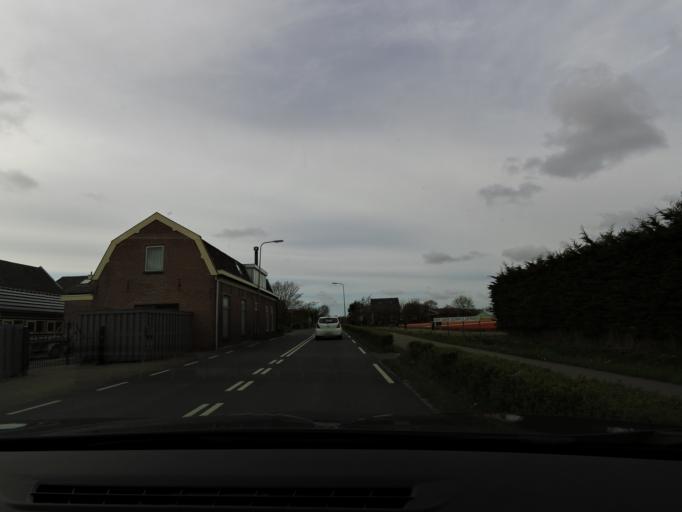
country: NL
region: South Holland
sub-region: Gemeente Lisse
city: Lisse
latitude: 52.2869
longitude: 4.5308
